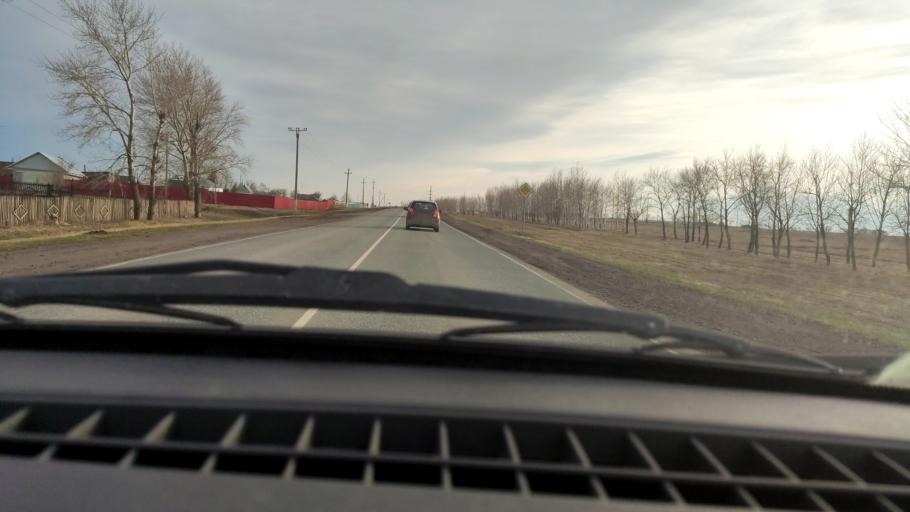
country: RU
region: Bashkortostan
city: Davlekanovo
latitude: 54.3886
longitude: 55.2008
